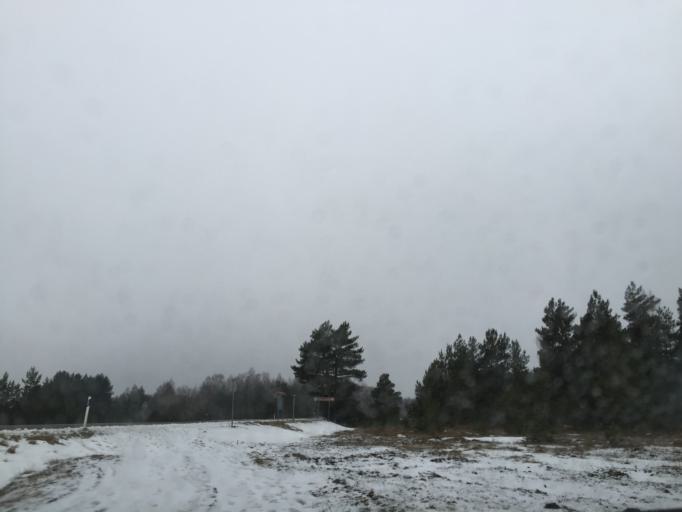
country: EE
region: Laeaene
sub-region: Lihula vald
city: Lihula
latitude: 58.6205
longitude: 23.6295
